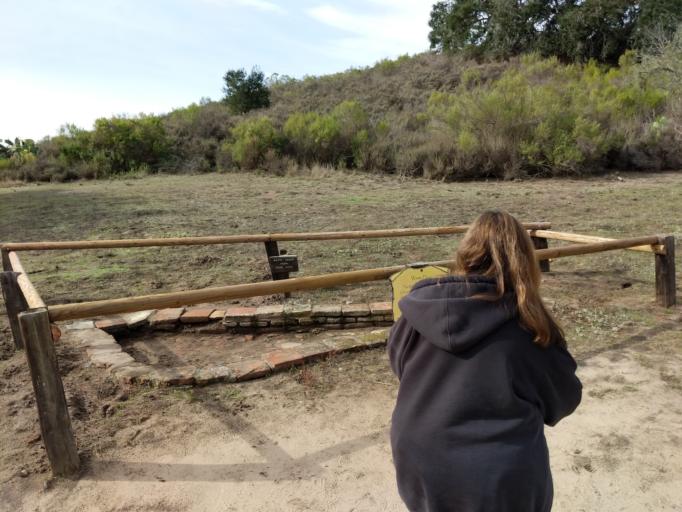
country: US
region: California
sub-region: Santa Barbara County
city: Mission Hills
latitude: 34.6717
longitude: -120.4228
